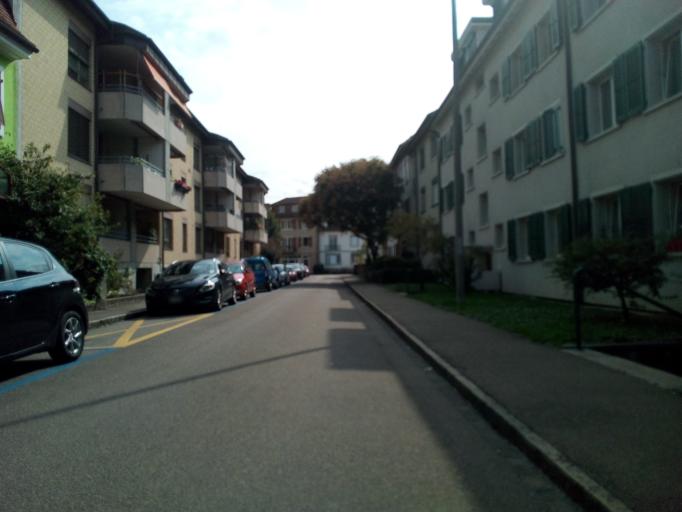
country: CH
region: Basel-Landschaft
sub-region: Bezirk Arlesheim
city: Birsfelden
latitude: 47.5563
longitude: 7.6197
